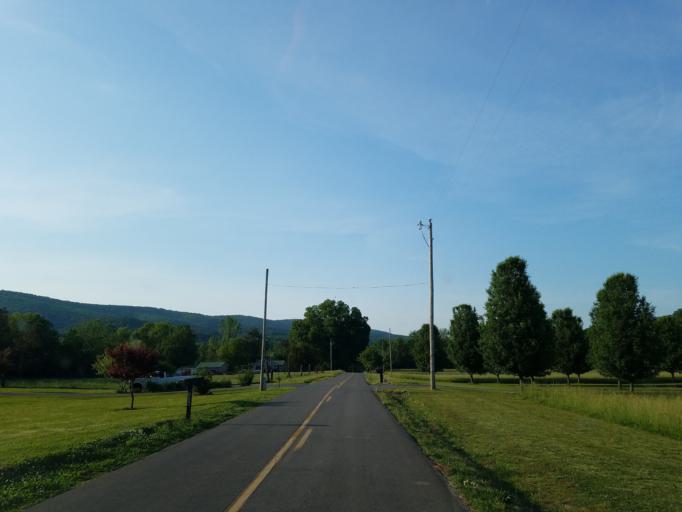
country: US
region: Georgia
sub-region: Gordon County
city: Calhoun
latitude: 34.5374
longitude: -85.1075
